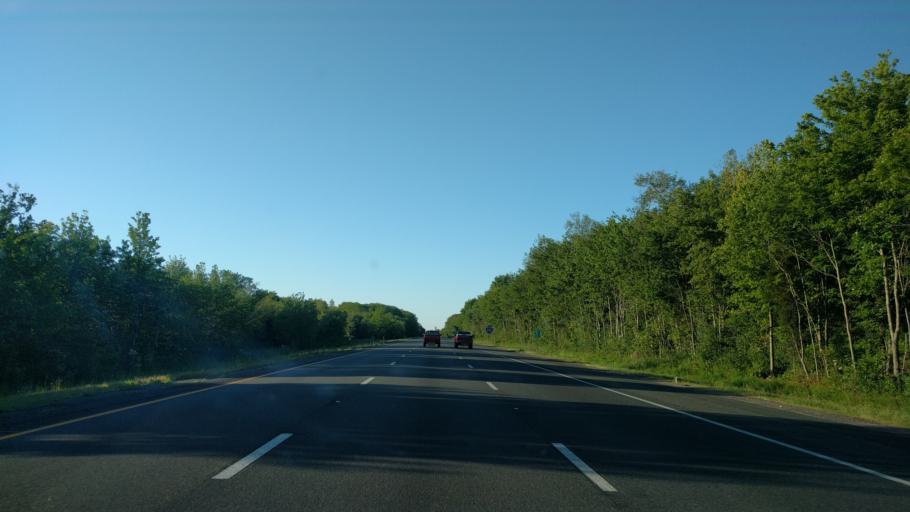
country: US
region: Massachusetts
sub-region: Worcester County
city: Milford
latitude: 42.1406
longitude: -71.4819
